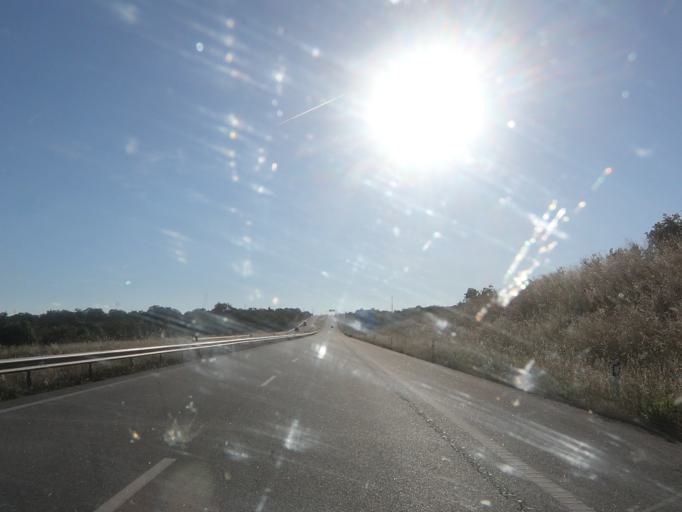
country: PT
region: Guarda
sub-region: Pinhel
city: Pinhel
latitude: 40.6036
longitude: -7.0506
